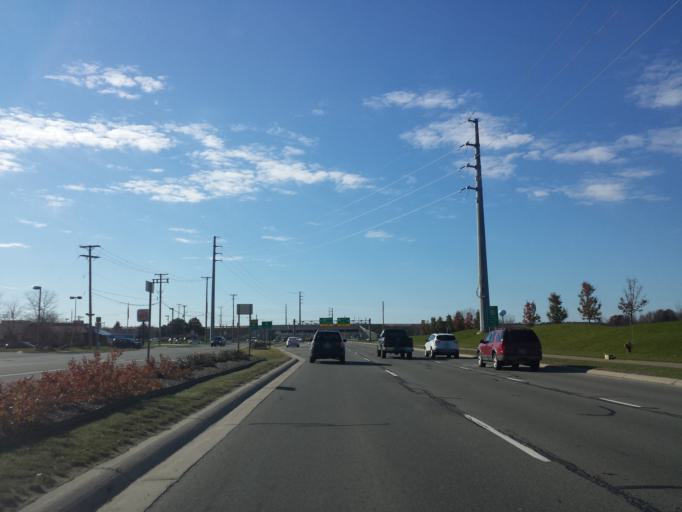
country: US
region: Michigan
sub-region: Livingston County
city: Brighton
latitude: 42.6340
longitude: -83.7444
